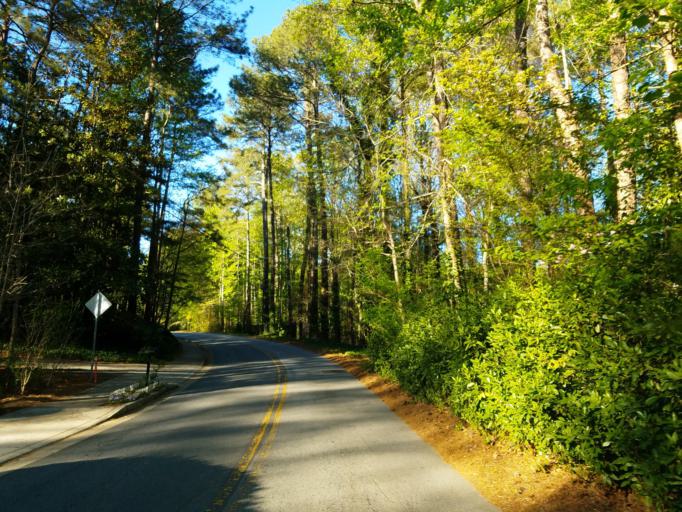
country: US
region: Georgia
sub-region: Cobb County
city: Vinings
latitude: 33.8576
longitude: -84.4656
